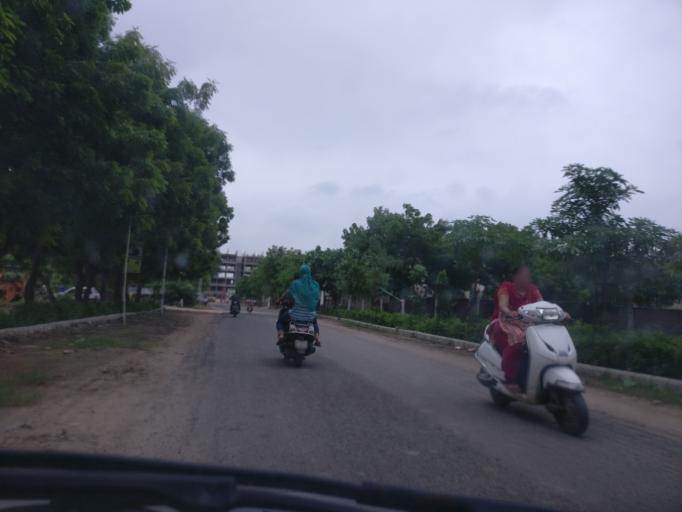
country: IN
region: Gujarat
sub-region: Ahmadabad
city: Naroda
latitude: 23.0553
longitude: 72.6630
